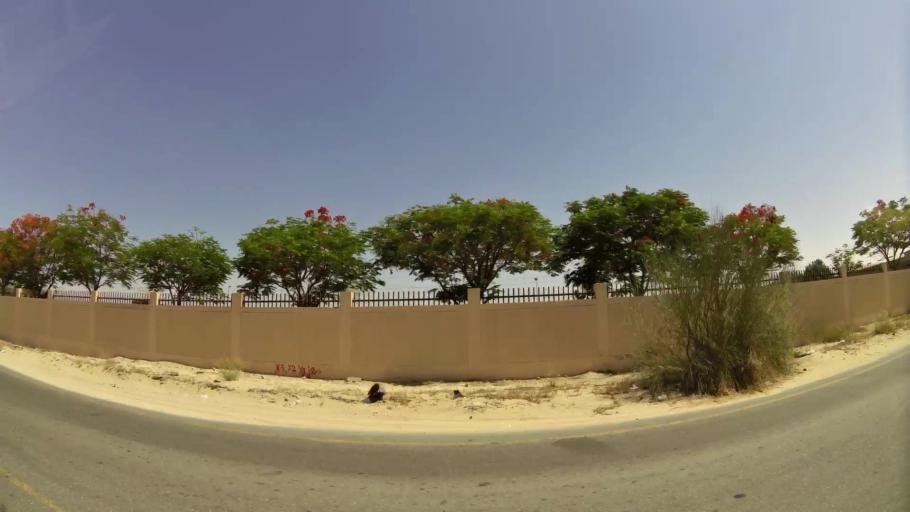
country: AE
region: Dubai
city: Dubai
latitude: 24.9898
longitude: 55.1927
